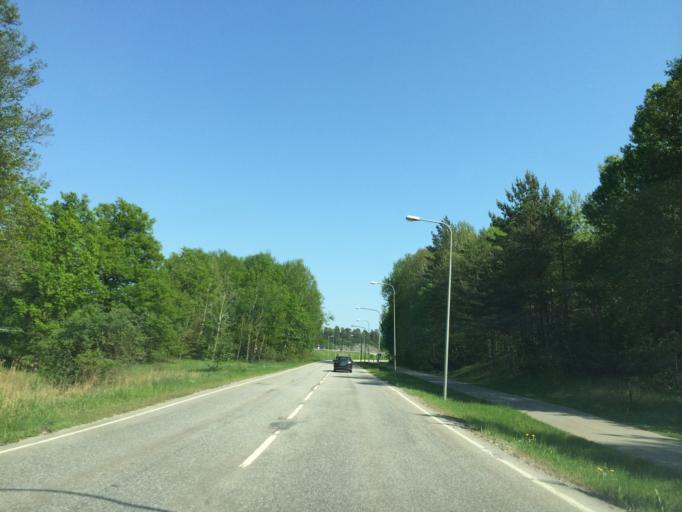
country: SE
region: Stockholm
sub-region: Nacka Kommun
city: Alta
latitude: 59.2616
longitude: 18.1529
